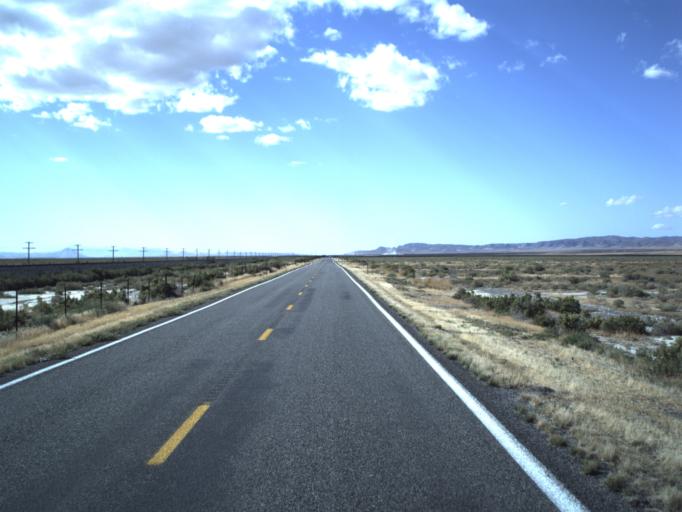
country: US
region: Utah
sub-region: Millard County
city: Delta
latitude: 39.0625
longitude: -112.7627
